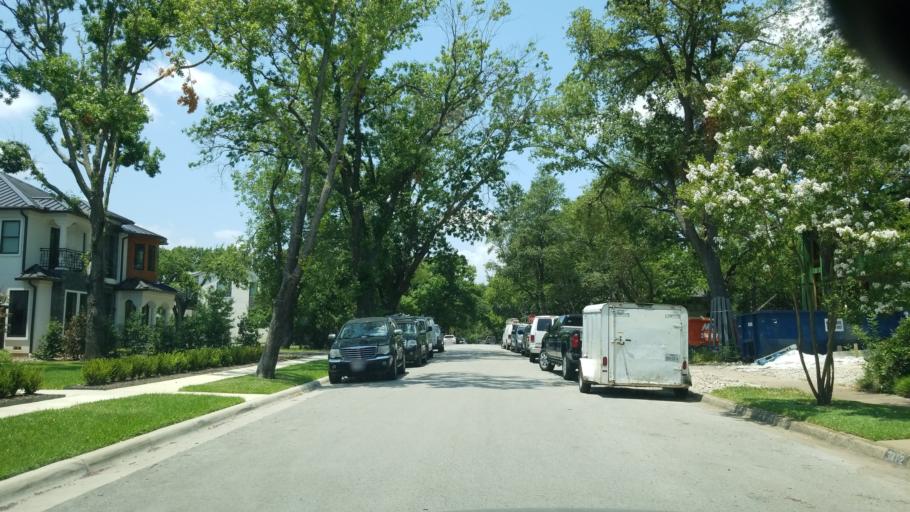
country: US
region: Texas
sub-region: Dallas County
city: Highland Park
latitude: 32.8281
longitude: -96.7883
